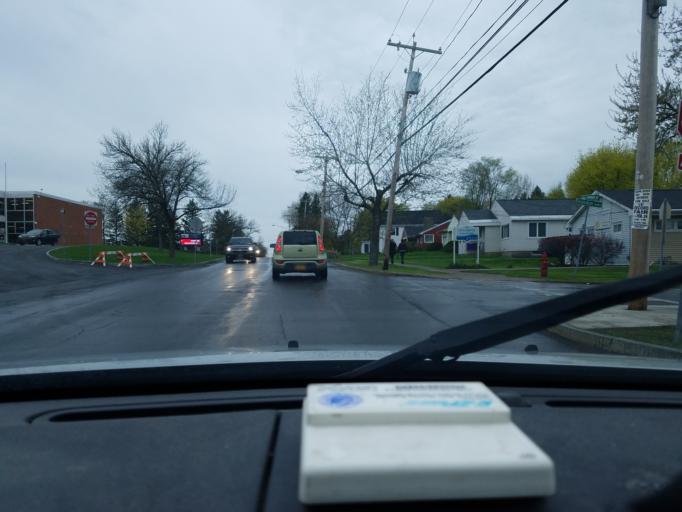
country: US
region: New York
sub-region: Onondaga County
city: East Syracuse
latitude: 43.0476
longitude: -76.0949
